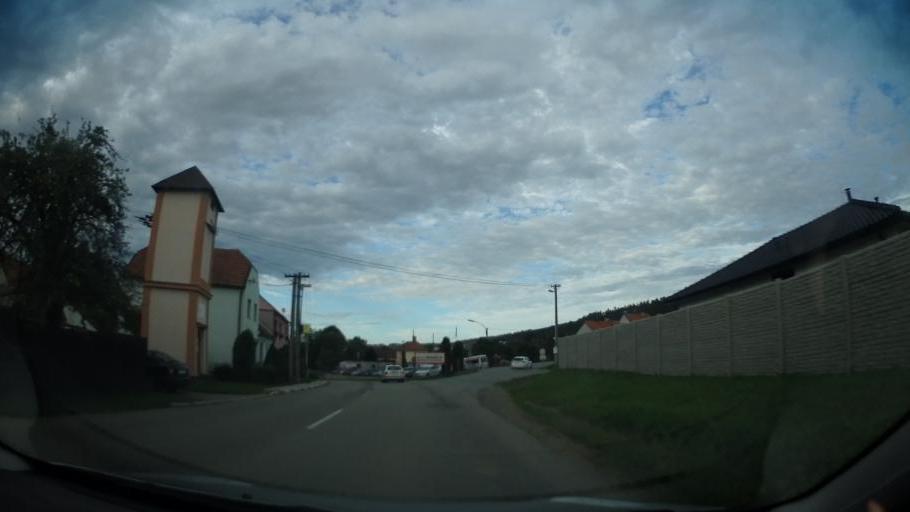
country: CZ
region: South Moravian
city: Velke Opatovice
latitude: 49.5456
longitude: 16.7080
